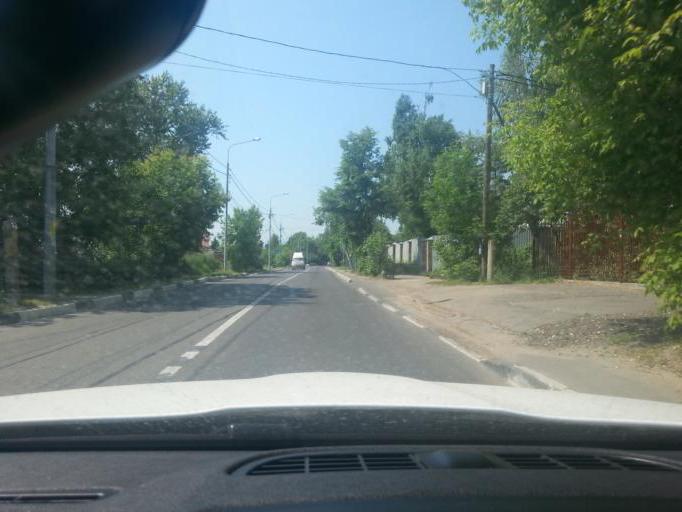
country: RU
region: Moskovskaya
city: Zheleznodorozhnyy
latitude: 55.7253
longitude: 38.0131
